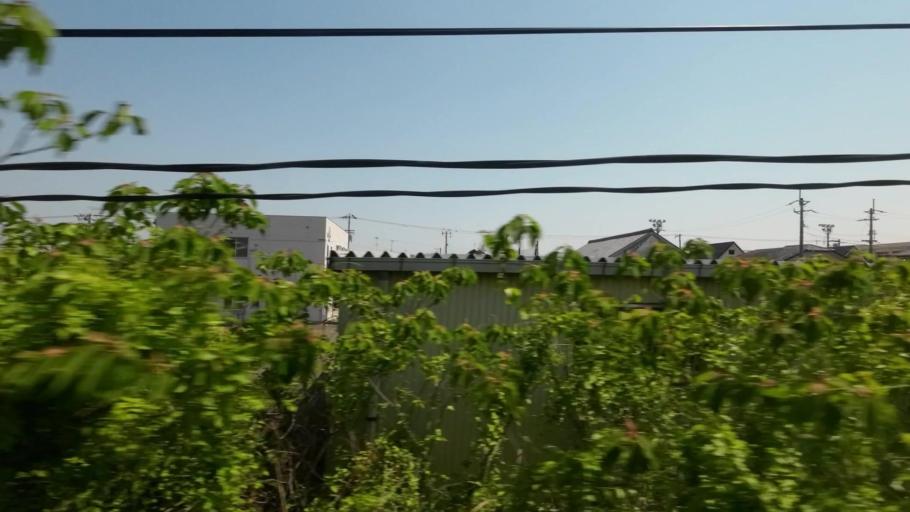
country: JP
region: Ehime
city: Saijo
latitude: 33.9363
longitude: 133.0798
